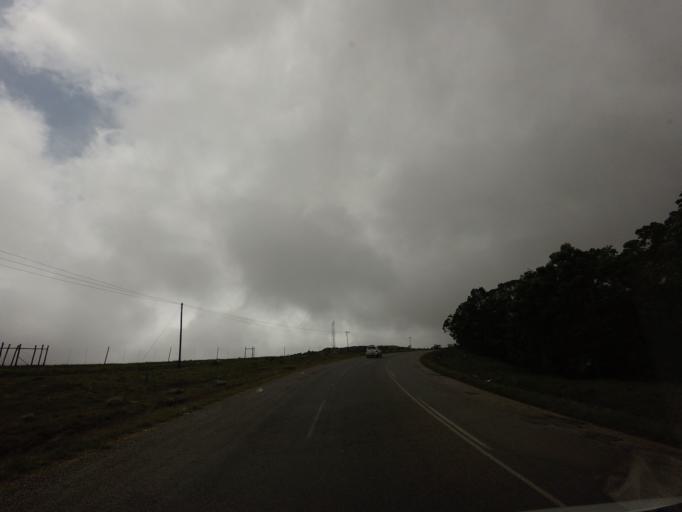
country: SZ
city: Darkton
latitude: -26.1484
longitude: 31.1314
